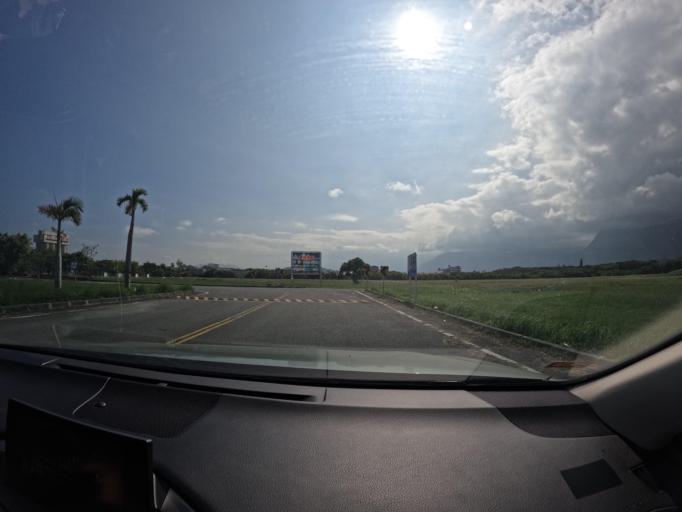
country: TW
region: Taiwan
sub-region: Hualien
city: Hualian
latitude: 24.0193
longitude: 121.6353
